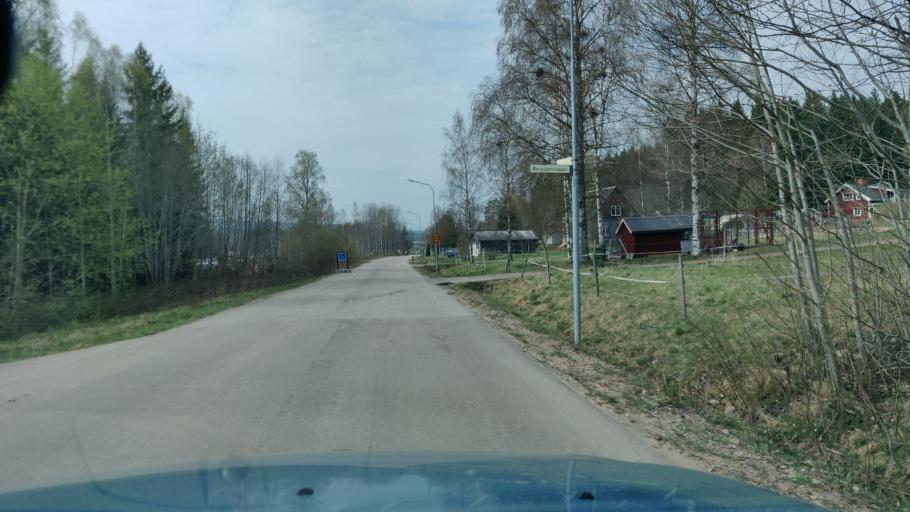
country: SE
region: Vaermland
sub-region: Munkfors Kommun
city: Munkfors
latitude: 59.8357
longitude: 13.5105
